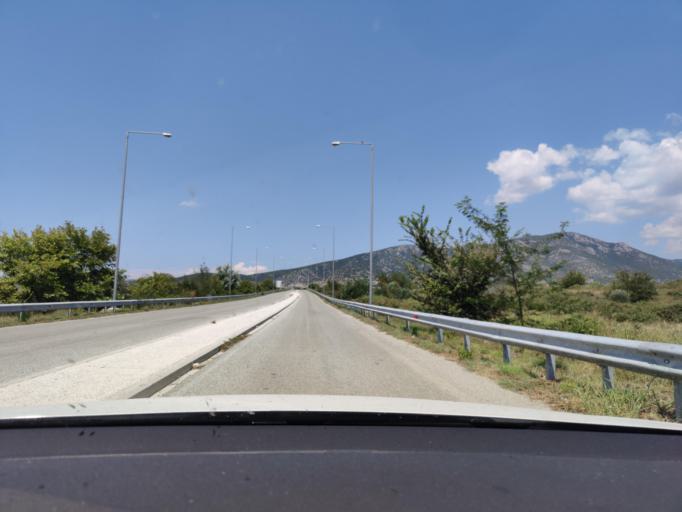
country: GR
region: East Macedonia and Thrace
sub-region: Nomos Kavalas
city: Paralia Ofryniou
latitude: 40.7827
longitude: 23.9564
